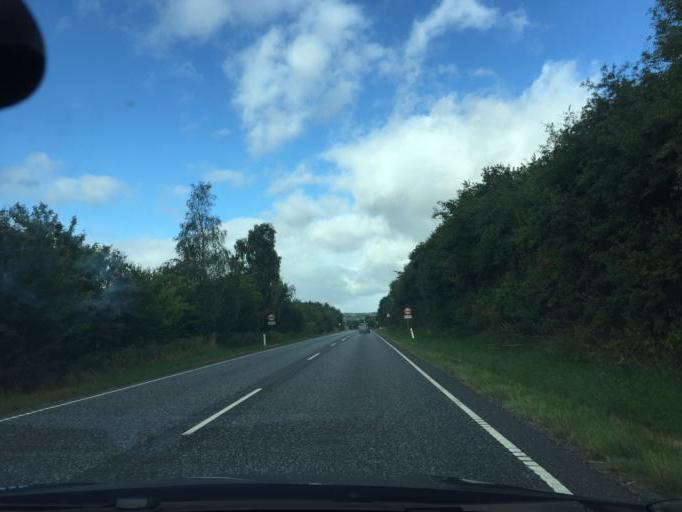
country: DK
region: South Denmark
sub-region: Vejle Kommune
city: Vejle
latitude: 55.7082
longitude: 9.4761
